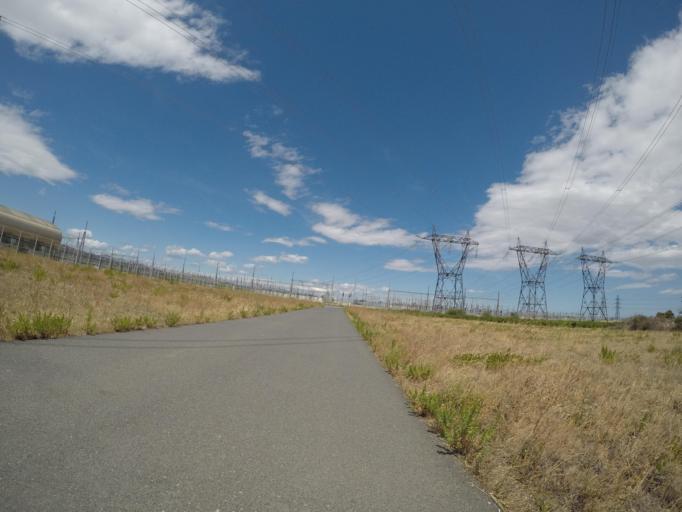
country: FR
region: Languedoc-Roussillon
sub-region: Departement des Pyrenees-Orientales
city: Baixas
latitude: 42.7300
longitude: 2.8033
